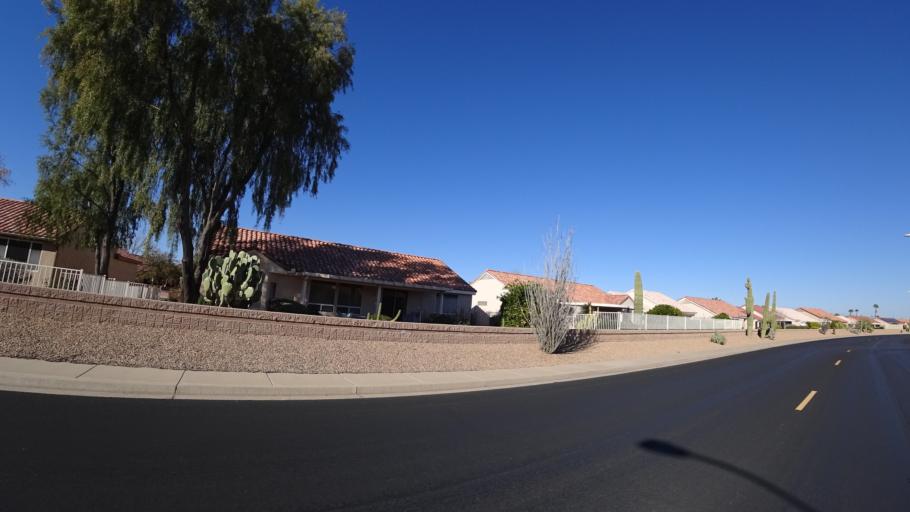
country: US
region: Arizona
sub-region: Maricopa County
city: Sun City West
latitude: 33.6934
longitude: -112.3761
